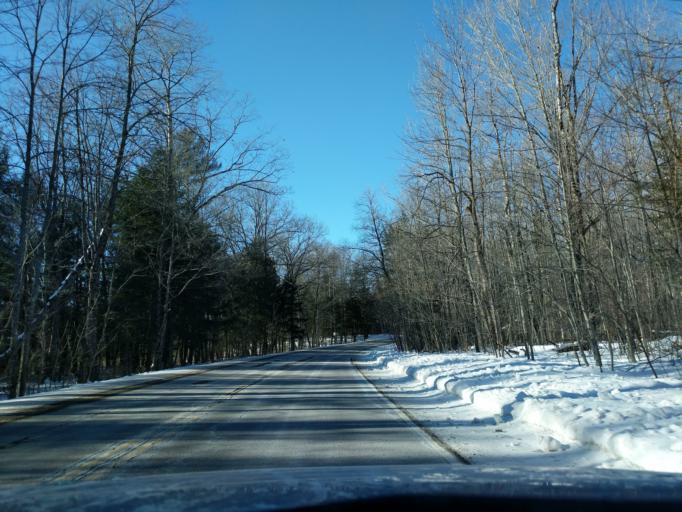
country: US
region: Wisconsin
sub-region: Menominee County
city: Keshena
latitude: 45.1163
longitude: -88.6543
